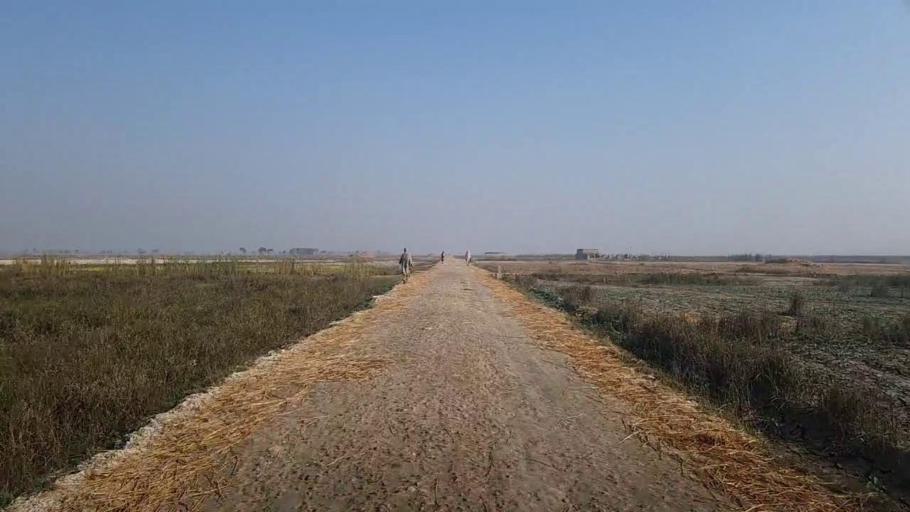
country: PK
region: Sindh
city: Radhan
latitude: 27.1333
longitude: 67.9039
